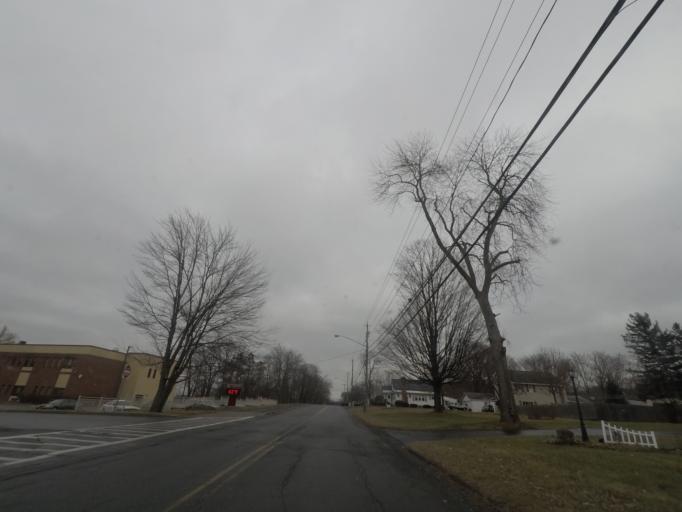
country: US
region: New York
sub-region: Saratoga County
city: Waterford
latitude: 42.7894
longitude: -73.6664
